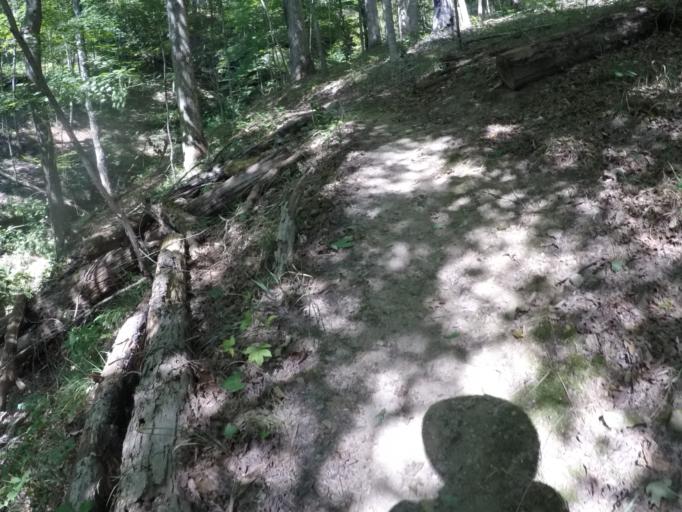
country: US
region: Ohio
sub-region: Lawrence County
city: Ironton
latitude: 38.6228
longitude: -82.6224
